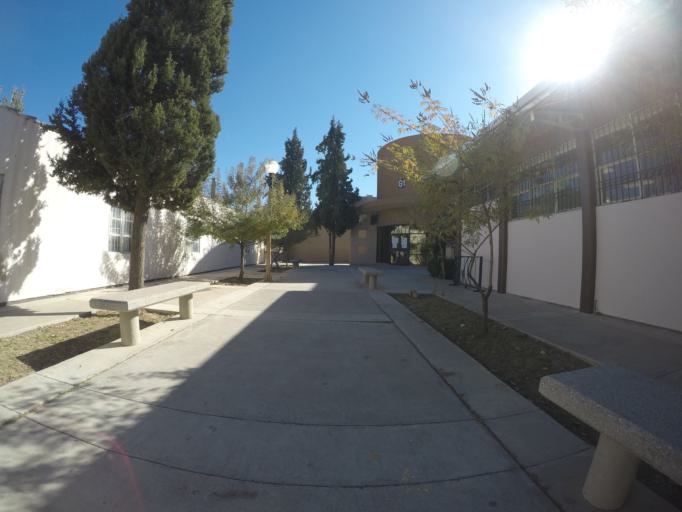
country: MX
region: Chihuahua
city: Ciudad Juarez
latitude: 31.7416
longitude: -106.4323
